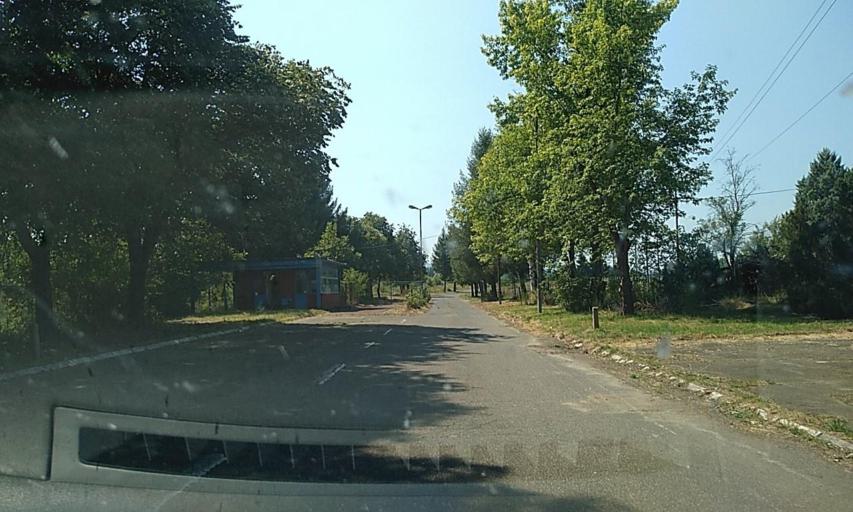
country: RS
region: Central Serbia
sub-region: Pcinjski Okrug
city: Vladicin Han
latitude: 42.6649
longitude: 22.0505
